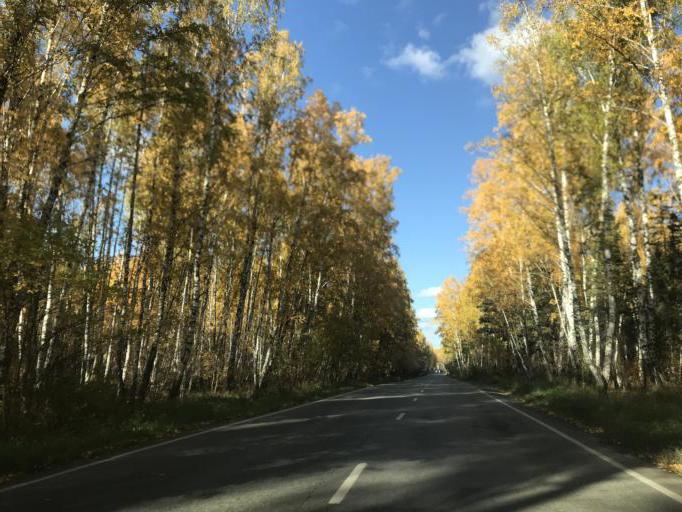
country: RU
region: Chelyabinsk
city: Dolgoderevenskoye
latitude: 55.2660
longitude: 61.3646
